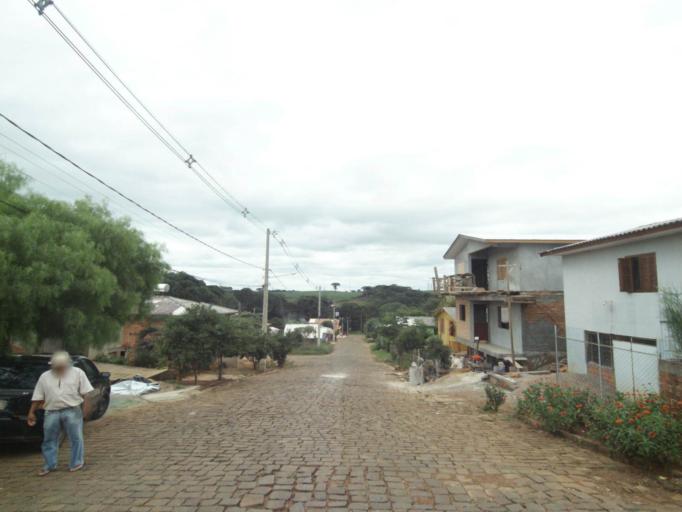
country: BR
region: Rio Grande do Sul
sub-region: Lagoa Vermelha
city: Lagoa Vermelha
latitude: -28.2133
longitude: -51.5060
